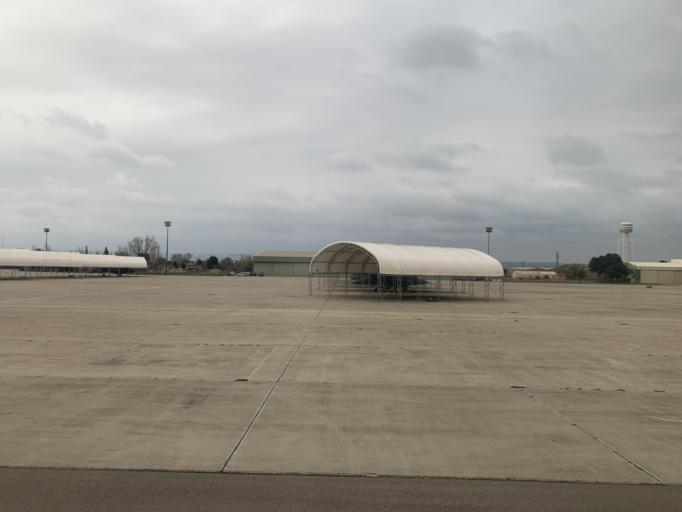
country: ES
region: Aragon
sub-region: Provincia de Zaragoza
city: Utebo
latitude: 41.6670
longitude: -1.0282
